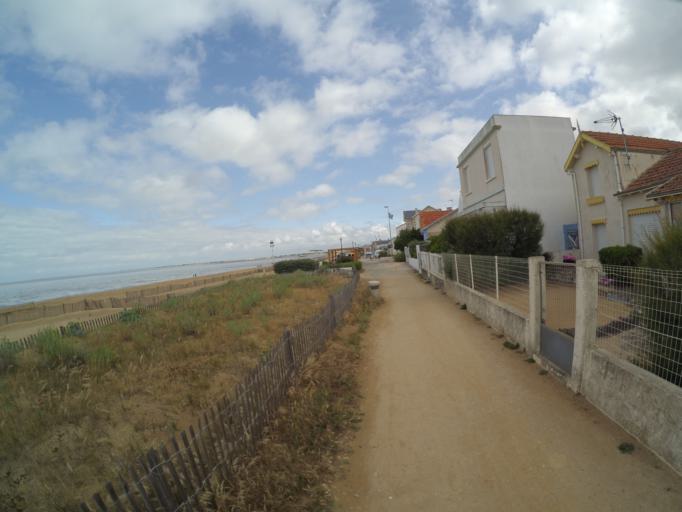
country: FR
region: Poitou-Charentes
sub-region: Departement de la Charente-Maritime
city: Chatelaillon-Plage
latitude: 46.0693
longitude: -1.0929
